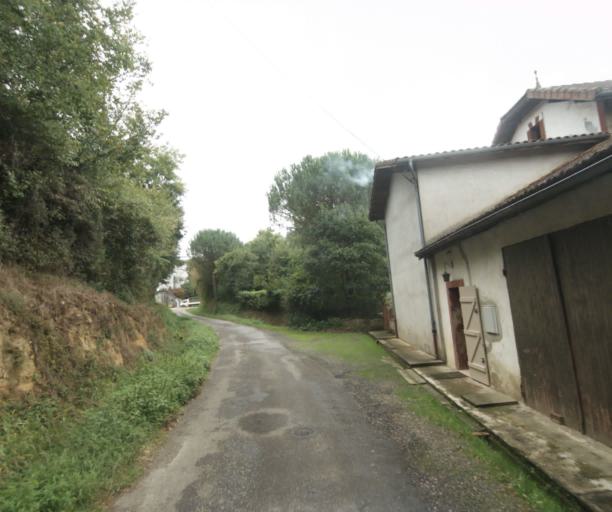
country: FR
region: Midi-Pyrenees
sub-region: Departement du Gers
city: Nogaro
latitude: 43.8173
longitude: -0.0847
